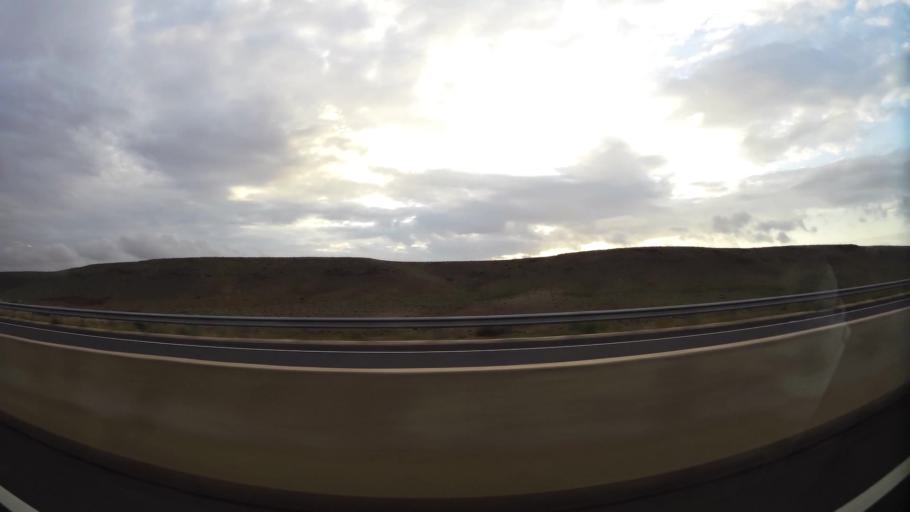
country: MA
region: Oriental
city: Taourirt
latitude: 34.4599
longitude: -3.0448
